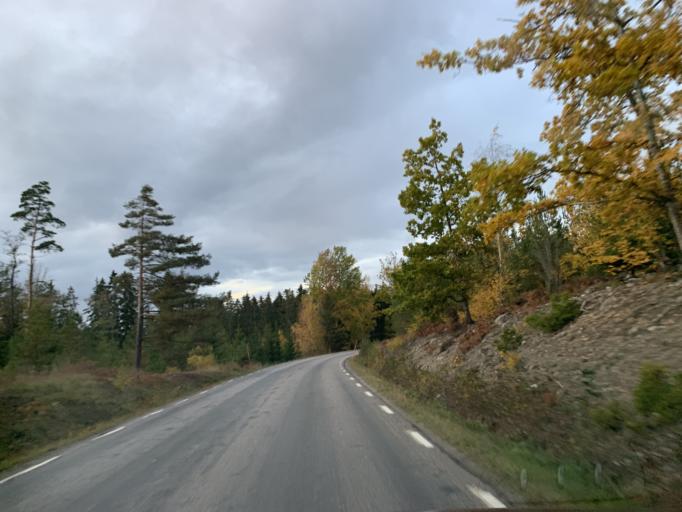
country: SE
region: Stockholm
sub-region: Nynashamns Kommun
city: Osmo
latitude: 58.9373
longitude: 17.7585
